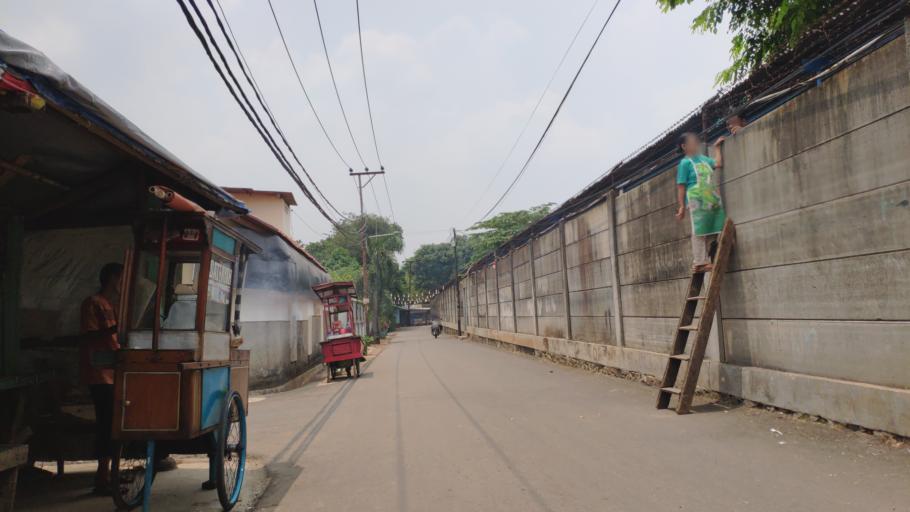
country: ID
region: Banten
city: South Tangerang
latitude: -6.2702
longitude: 106.7670
